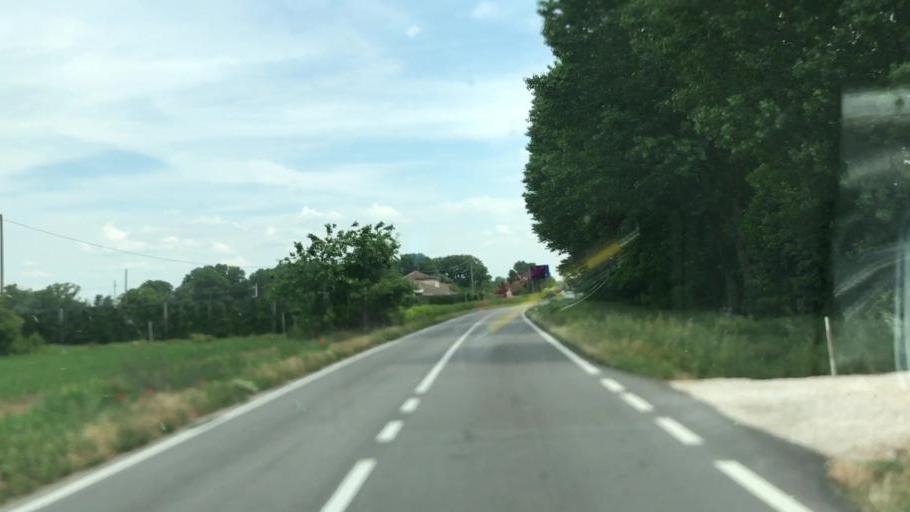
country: IT
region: Lombardy
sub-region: Provincia di Mantova
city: Bagnolo San Vito
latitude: 45.1248
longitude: 10.8856
